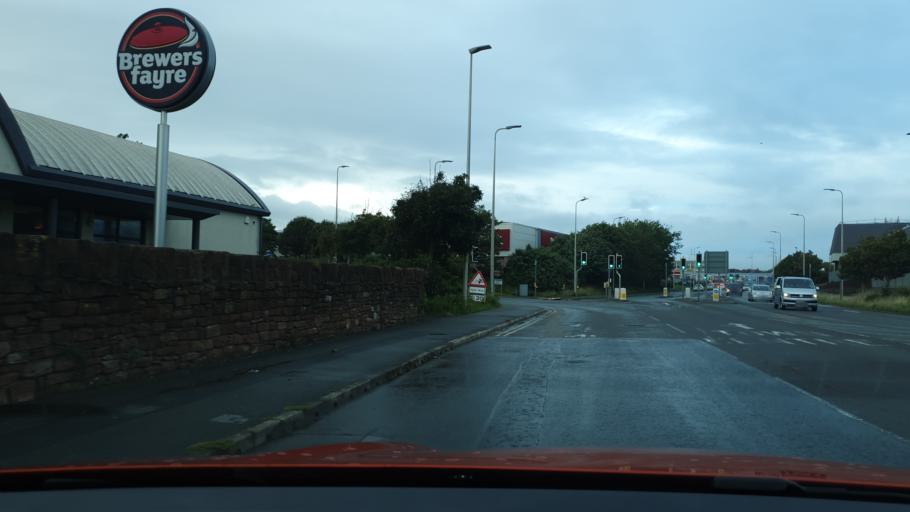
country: GB
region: England
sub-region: Cumbria
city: Barrow in Furness
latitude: 54.1125
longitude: -3.2386
